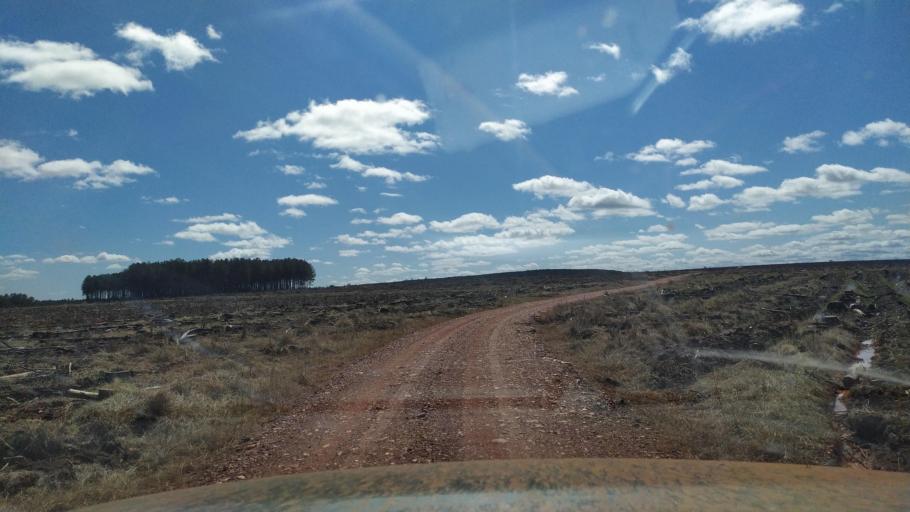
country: AR
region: Corrientes
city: Gobernador Ingeniero Valentin Virasoro
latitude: -28.2977
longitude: -56.0533
